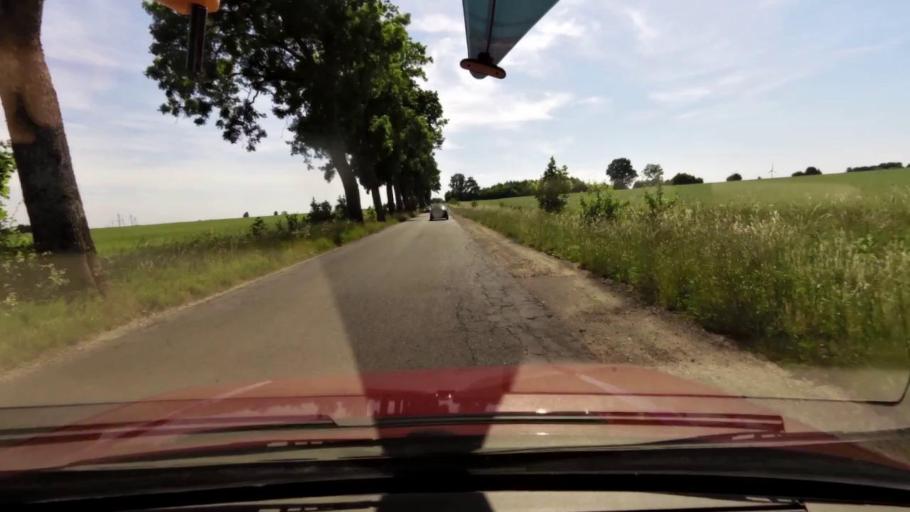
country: PL
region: Pomeranian Voivodeship
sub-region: Powiat slupski
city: Kobylnica
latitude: 54.3998
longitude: 16.9944
